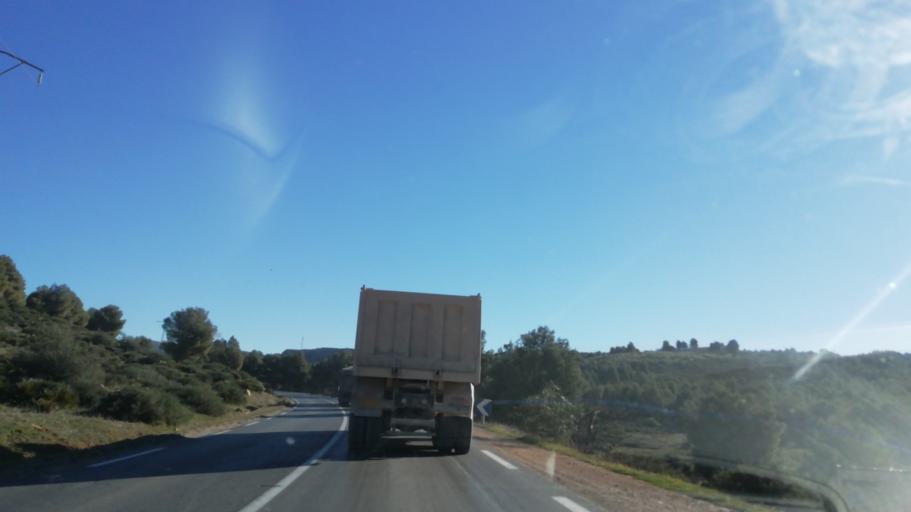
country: DZ
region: Tlemcen
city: Chetouane
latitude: 34.8939
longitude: -1.2462
